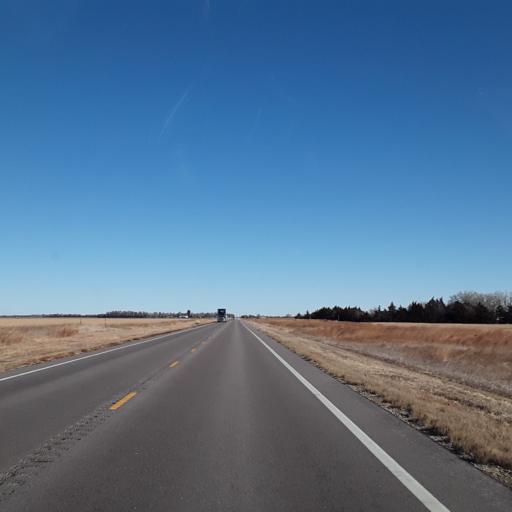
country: US
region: Kansas
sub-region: Pawnee County
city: Larned
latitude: 38.1034
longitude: -99.2031
